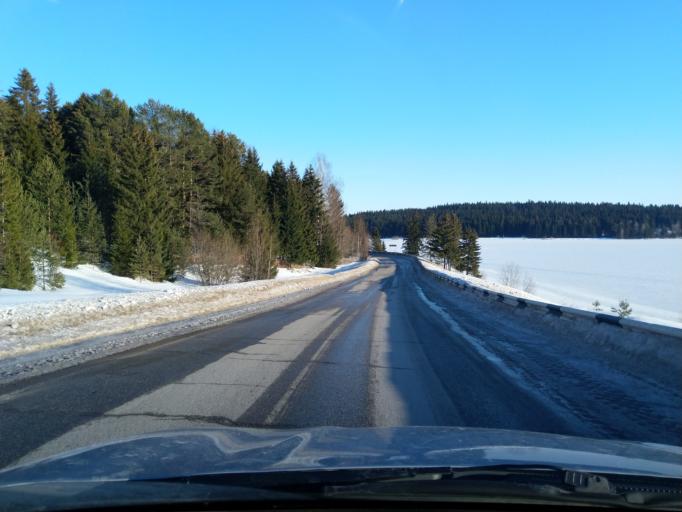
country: RU
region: Perm
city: Polazna
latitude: 58.3052
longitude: 56.4285
